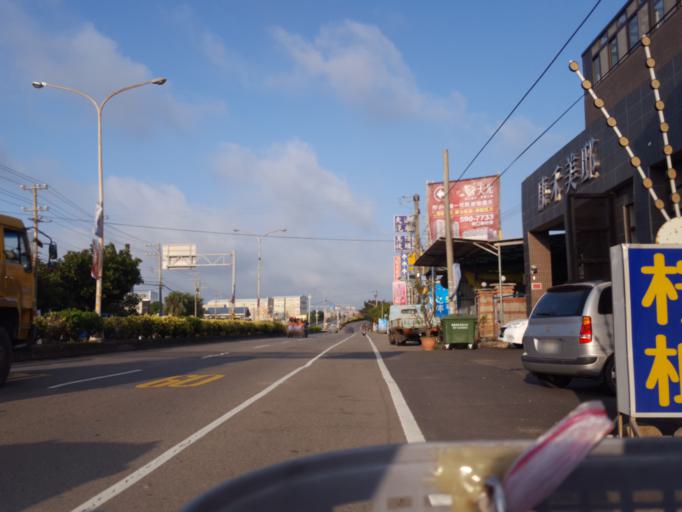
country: TW
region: Taiwan
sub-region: Hsinchu
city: Zhubei
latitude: 24.8841
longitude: 121.0131
